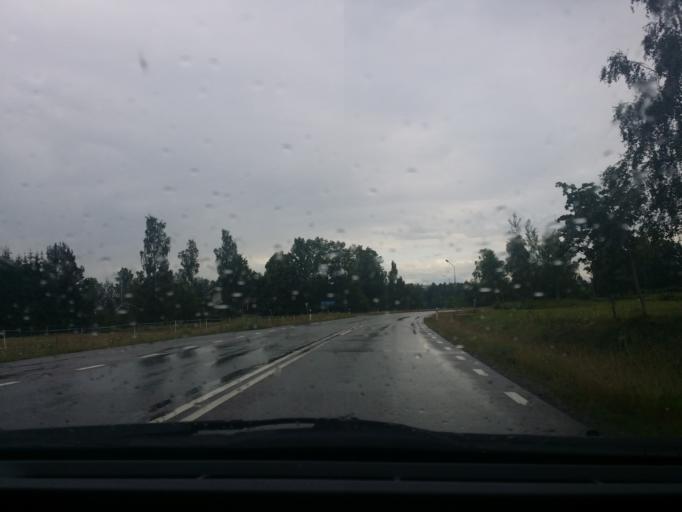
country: SE
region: OErebro
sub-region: Lindesbergs Kommun
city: Fellingsbro
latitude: 59.4458
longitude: 15.5952
